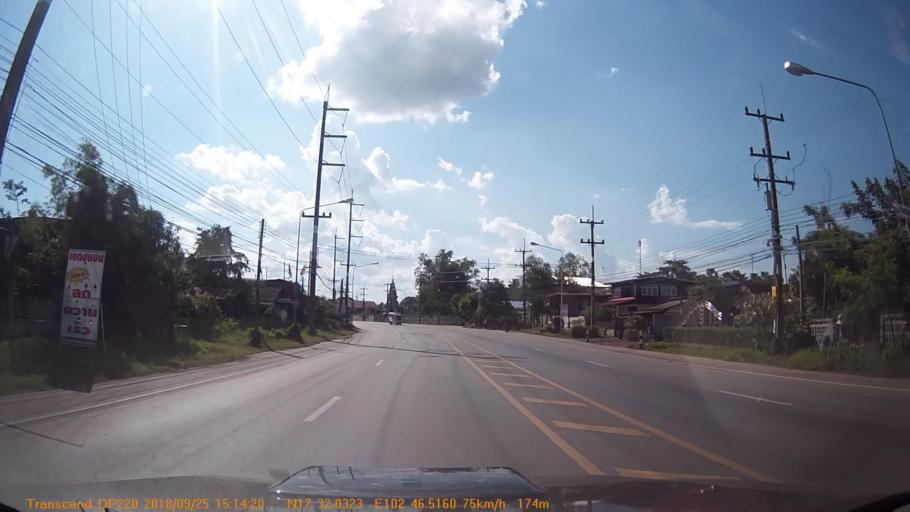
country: TH
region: Changwat Udon Thani
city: Udon Thani
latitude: 17.5340
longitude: 102.7747
